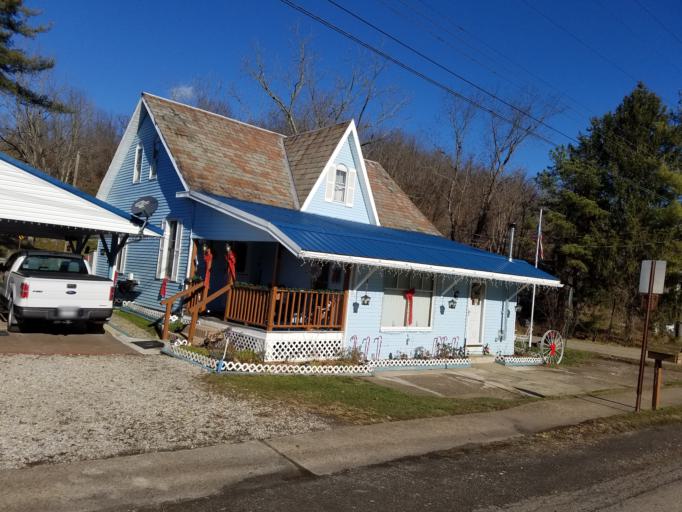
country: US
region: Ohio
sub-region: Belmont County
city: Barnesville
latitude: 40.0615
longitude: -81.1659
